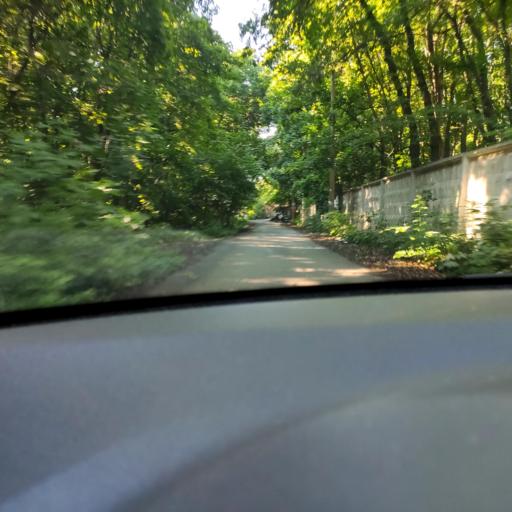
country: RU
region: Samara
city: Samara
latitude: 53.2611
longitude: 50.2485
